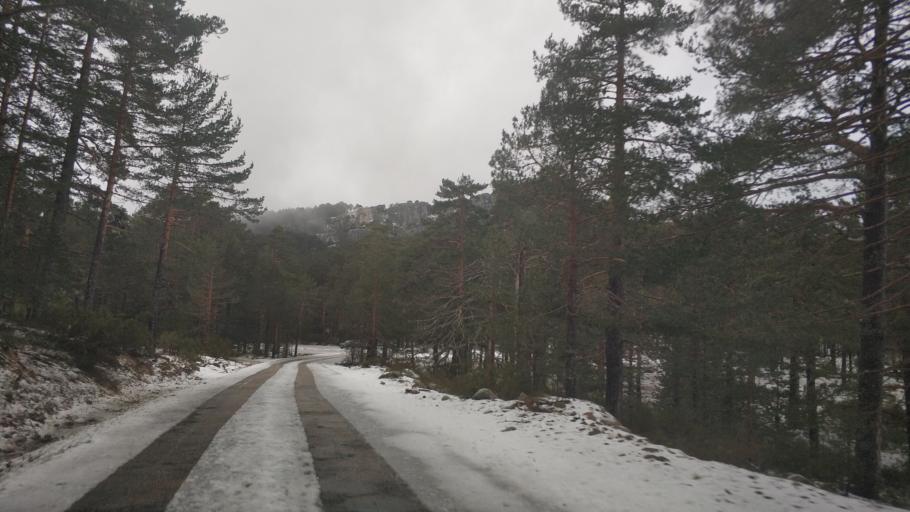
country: ES
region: Castille and Leon
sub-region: Provincia de Burgos
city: Neila
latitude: 42.0458
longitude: -3.0334
